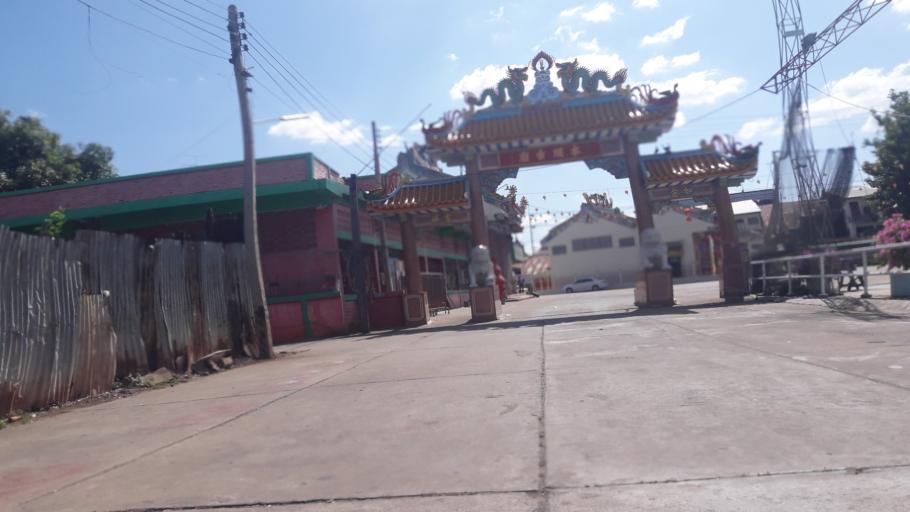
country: TH
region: Phichit
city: Thap Khlo
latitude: 16.1695
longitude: 100.5776
